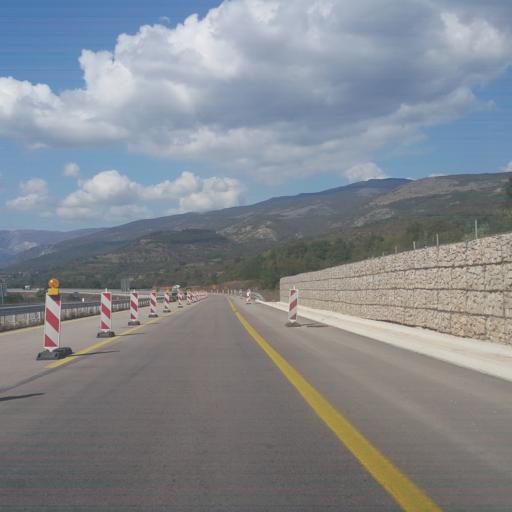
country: RS
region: Central Serbia
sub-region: Pirotski Okrug
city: Bela Palanka
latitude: 43.2523
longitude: 22.2698
